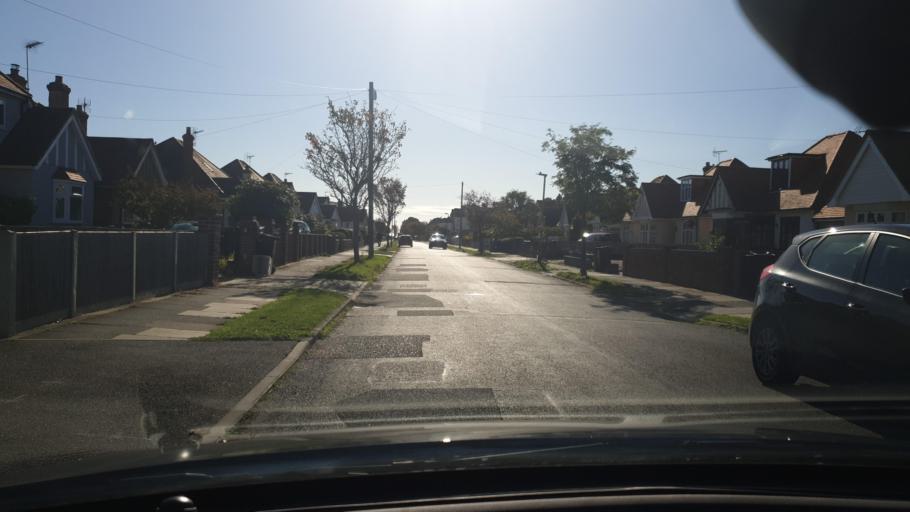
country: GB
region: England
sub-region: Essex
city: Clacton-on-Sea
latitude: 51.8044
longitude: 1.1894
